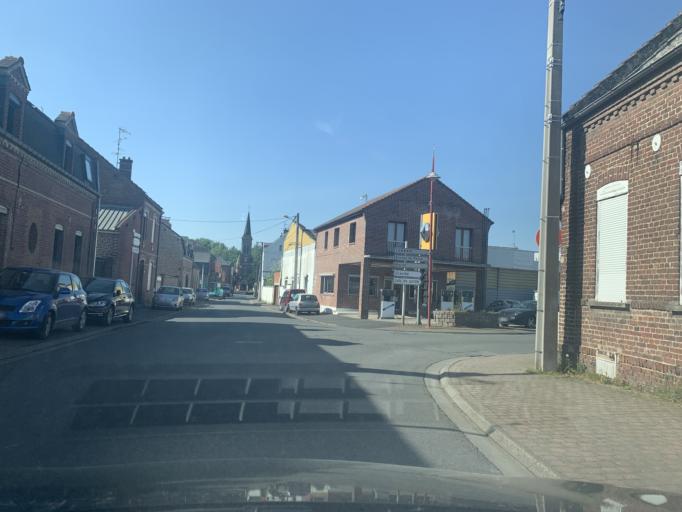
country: FR
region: Nord-Pas-de-Calais
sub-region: Departement du Nord
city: Proville
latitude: 50.1618
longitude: 3.2083
